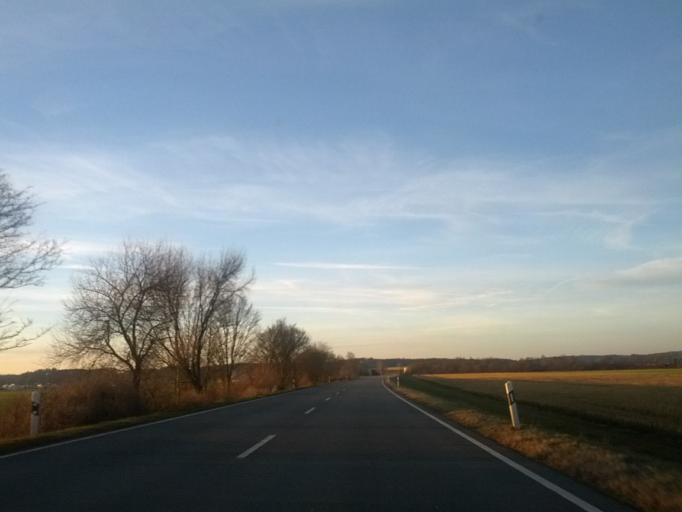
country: DE
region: Baden-Wuerttemberg
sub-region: Tuebingen Region
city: Berkheim
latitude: 48.0399
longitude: 10.1062
